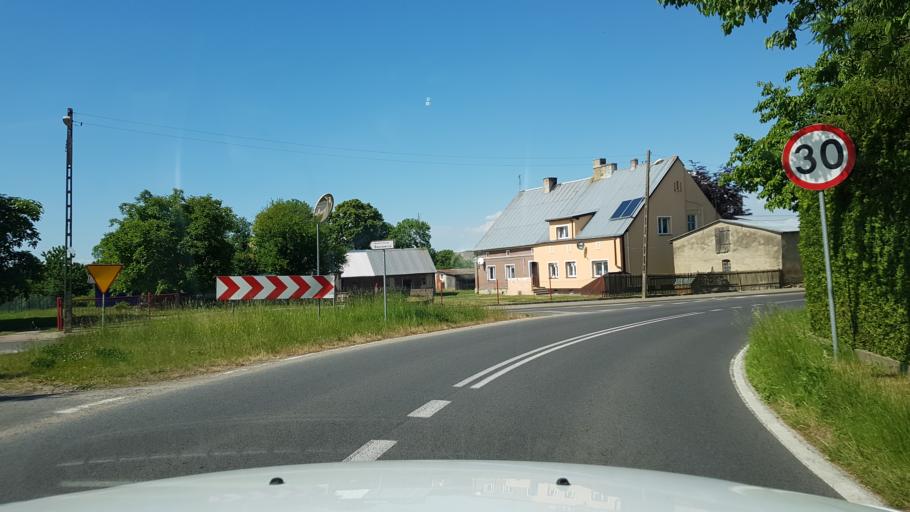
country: PL
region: West Pomeranian Voivodeship
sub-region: Powiat gryfinski
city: Banie
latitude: 53.0799
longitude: 14.6137
